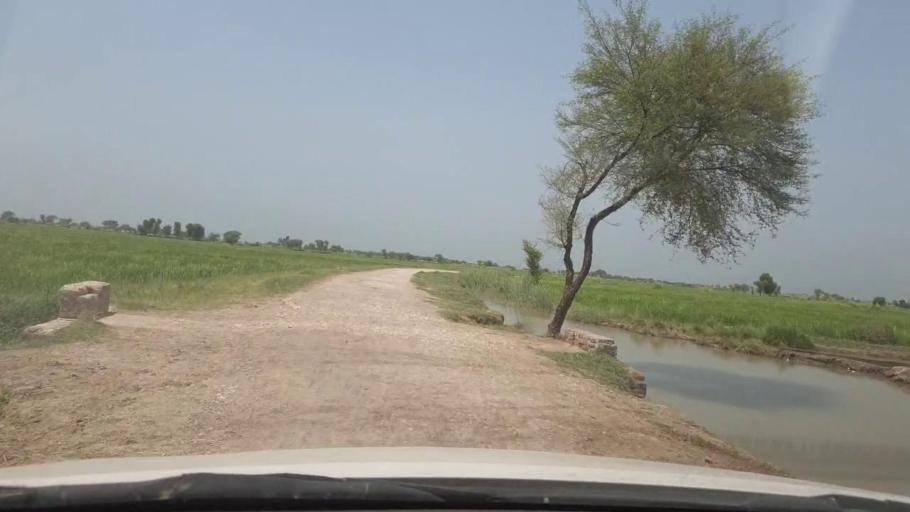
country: PK
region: Sindh
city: Shikarpur
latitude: 28.0736
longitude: 68.5742
